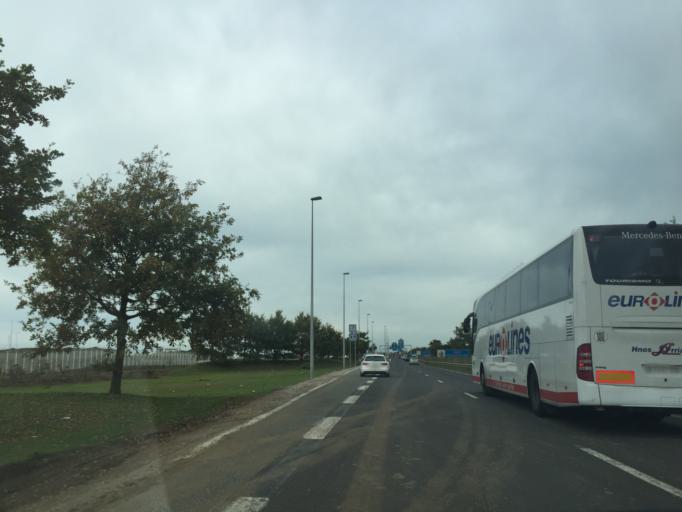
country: FR
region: Nord-Pas-de-Calais
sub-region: Departement du Pas-de-Calais
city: Frethun
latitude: 50.9323
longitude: 1.8178
